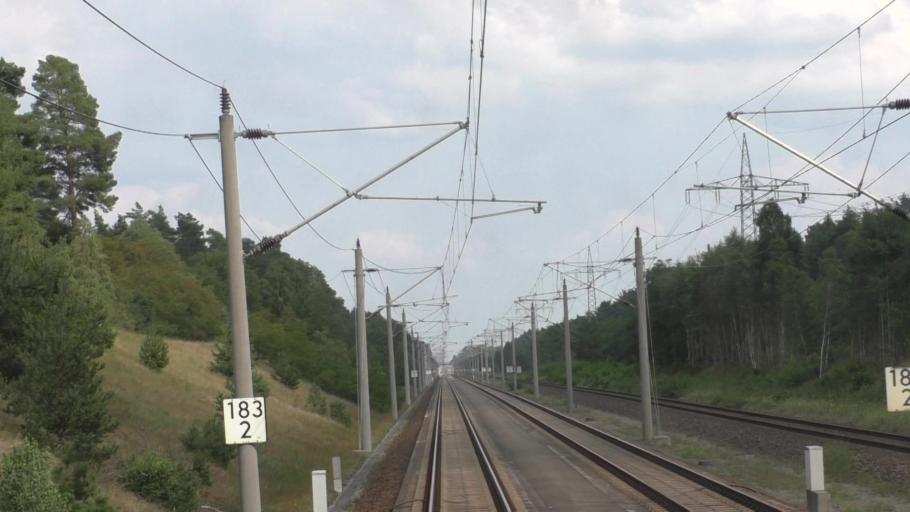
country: DE
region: Saxony-Anhalt
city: Schollene
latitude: 52.5904
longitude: 12.1737
